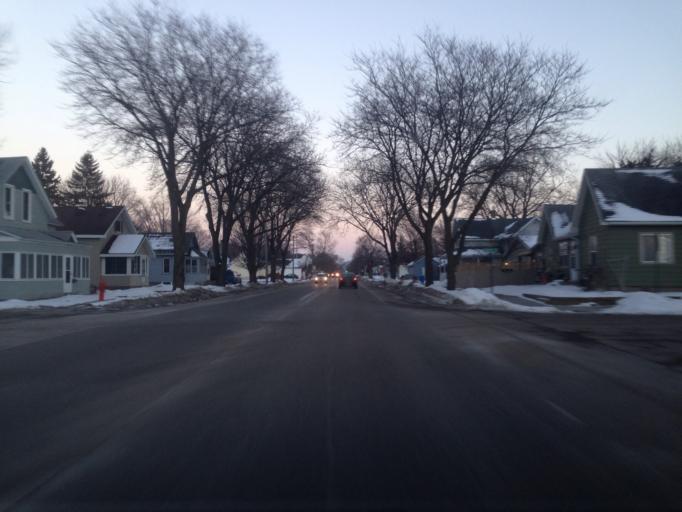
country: US
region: Minnesota
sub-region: Winona County
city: Winona
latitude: 44.0465
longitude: -91.6550
